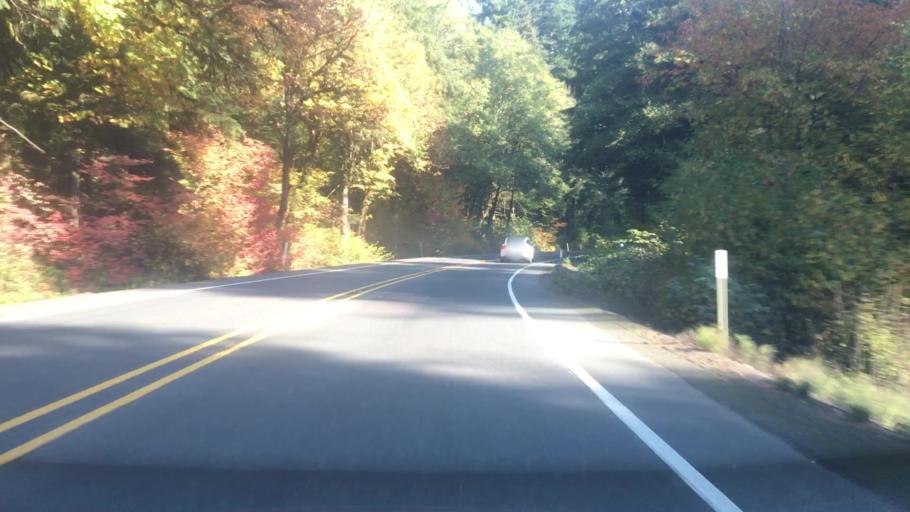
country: US
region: Oregon
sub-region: Lincoln County
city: Rose Lodge
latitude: 45.0558
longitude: -123.7552
